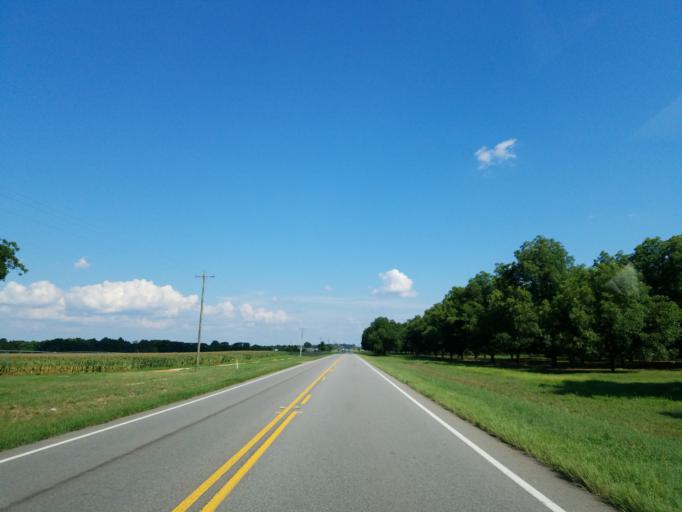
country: US
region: Georgia
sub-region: Peach County
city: Fort Valley
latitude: 32.6160
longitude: -83.9591
